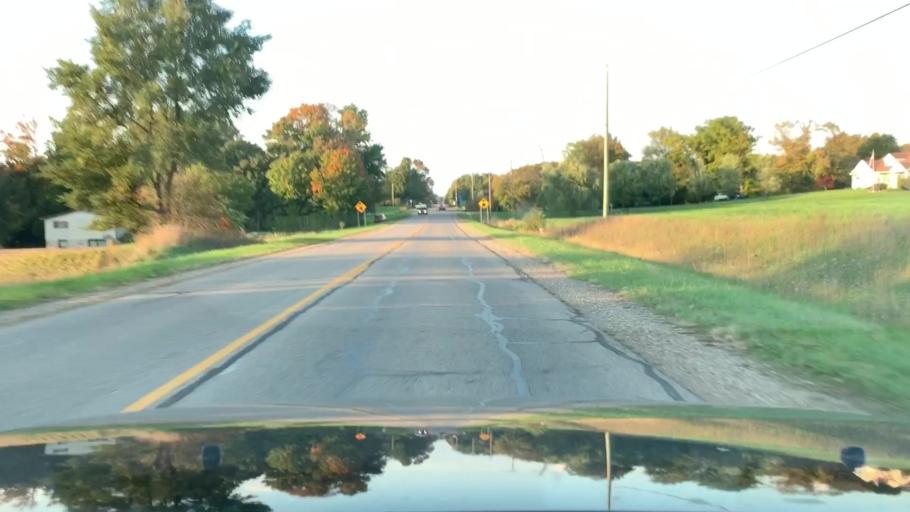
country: US
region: Michigan
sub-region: Ottawa County
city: Hudsonville
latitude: 42.8084
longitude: -85.8420
